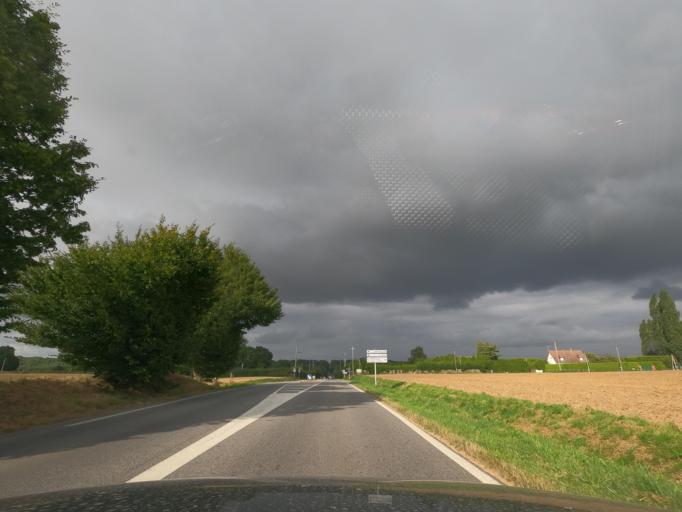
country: FR
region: Haute-Normandie
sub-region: Departement de l'Eure
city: Menneval
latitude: 49.1172
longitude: 0.6247
